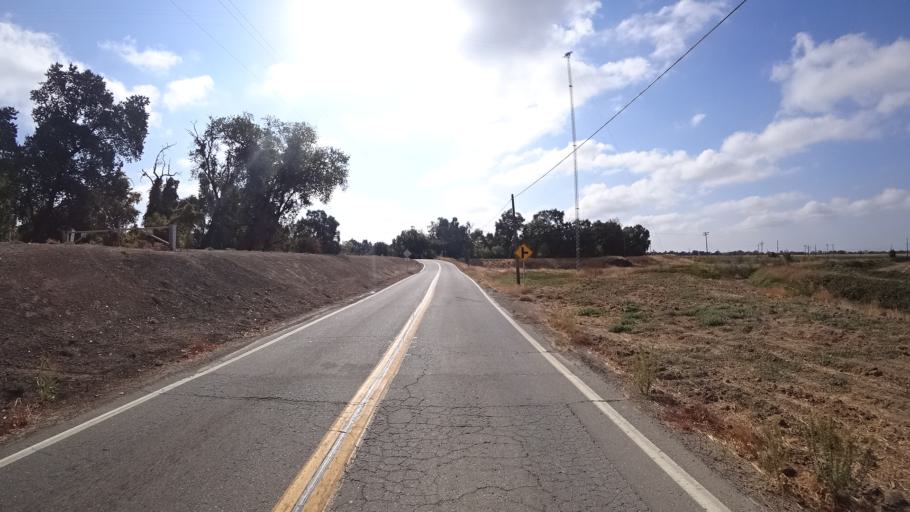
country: US
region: California
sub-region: Yolo County
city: Woodland
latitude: 38.8036
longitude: -121.7243
